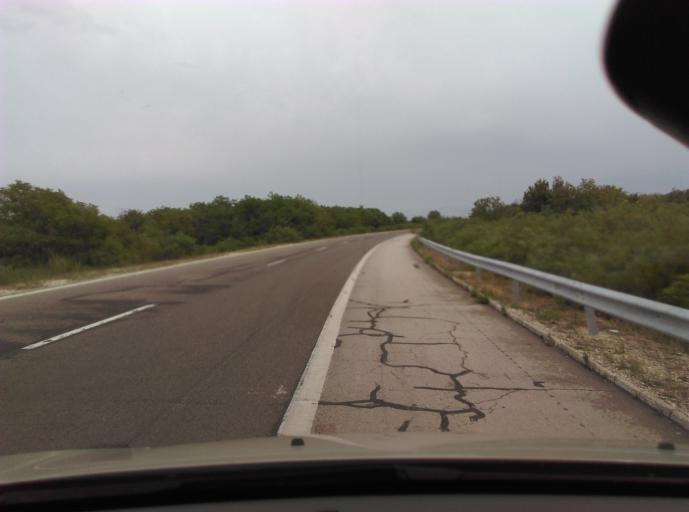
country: BG
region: Stara Zagora
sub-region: Obshtina Chirpan
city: Chirpan
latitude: 42.1932
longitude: 25.2335
